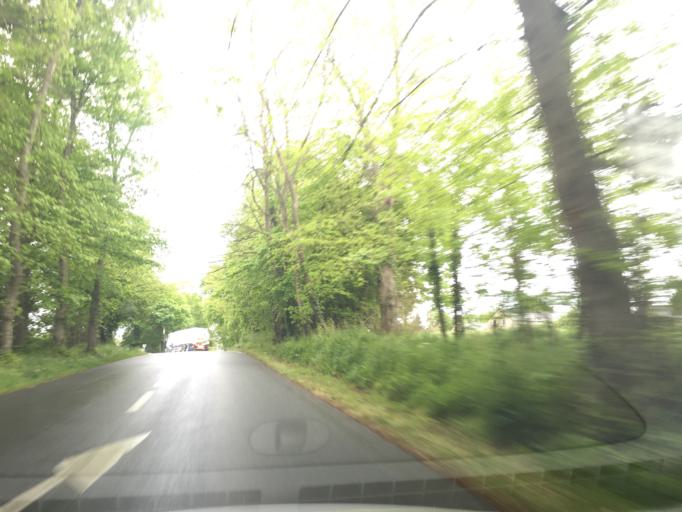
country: FR
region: Brittany
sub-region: Departement des Cotes-d'Armor
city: Crehen
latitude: 48.5393
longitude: -2.2278
